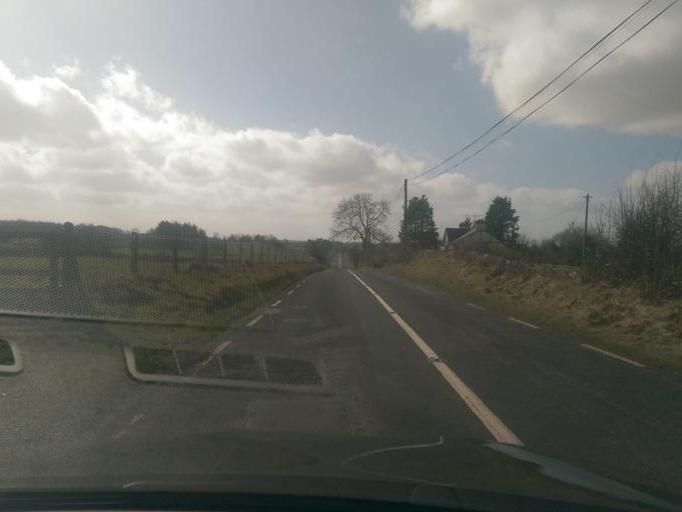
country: IE
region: Connaught
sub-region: County Galway
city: Athenry
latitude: 53.4125
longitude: -8.6250
